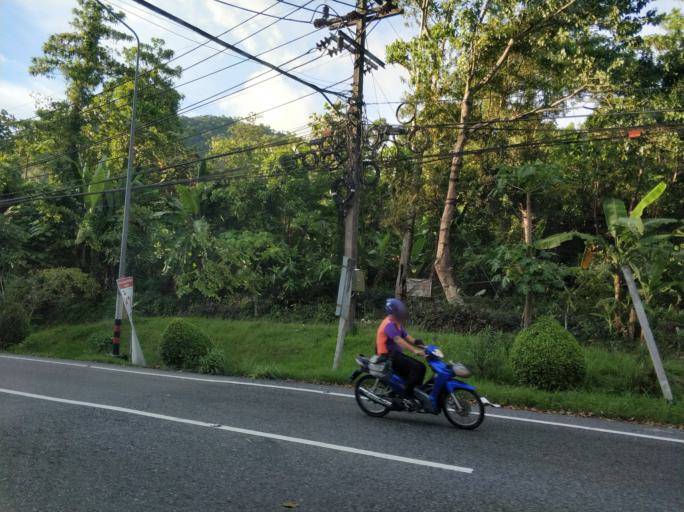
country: TH
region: Phuket
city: Kathu
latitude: 7.9028
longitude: 98.3209
